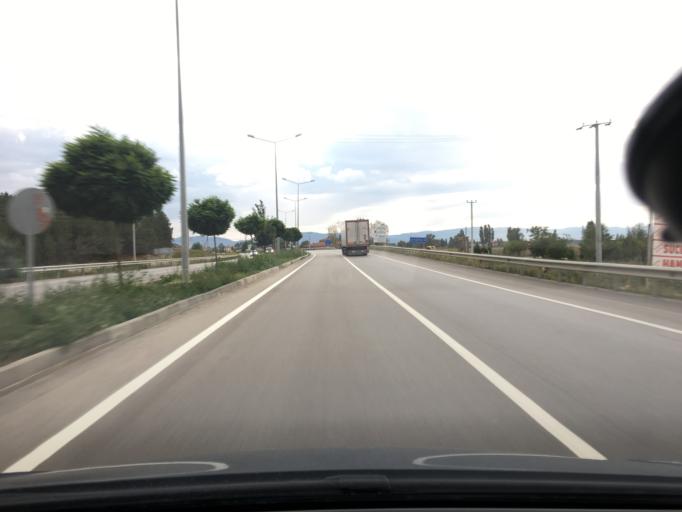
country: TR
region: Afyonkarahisar
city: Sincanli
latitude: 38.7897
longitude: 30.3810
